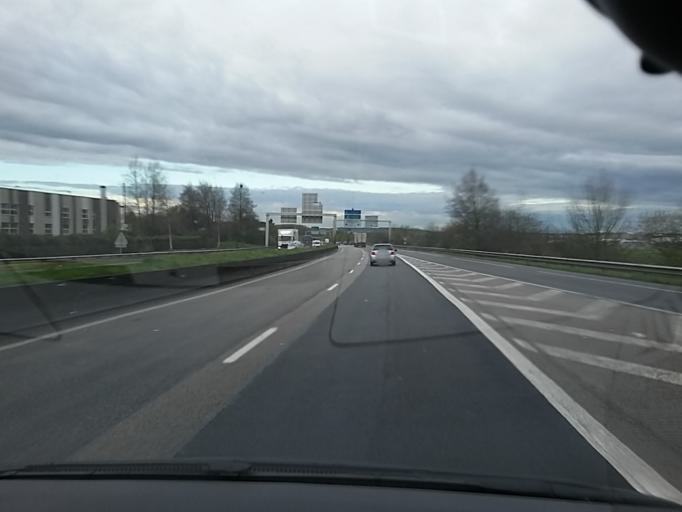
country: FR
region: Picardie
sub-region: Departement de la Somme
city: Poulainville
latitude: 49.9268
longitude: 2.3017
